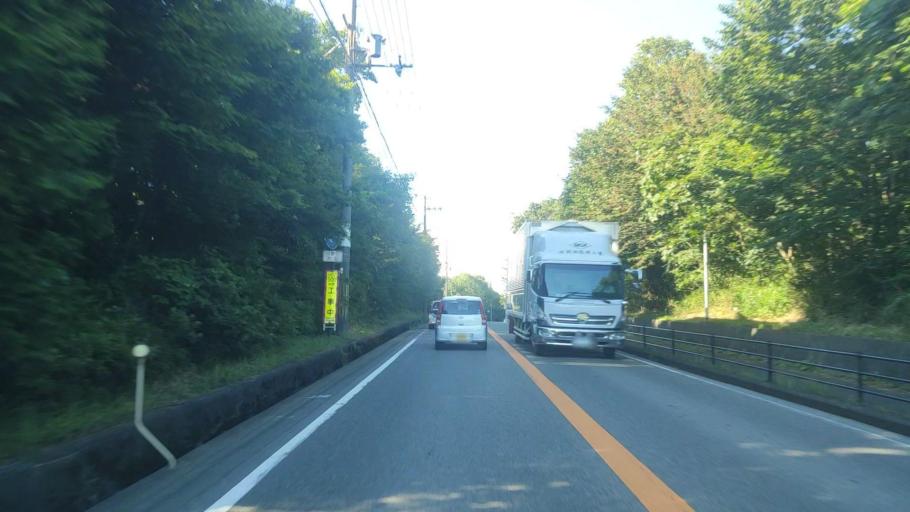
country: JP
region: Shiga Prefecture
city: Hino
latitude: 35.0267
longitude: 136.2392
